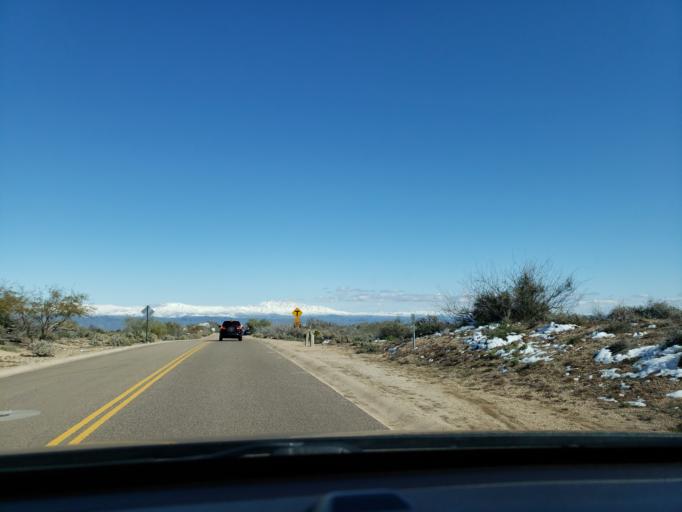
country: US
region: Arizona
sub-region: Maricopa County
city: Rio Verde
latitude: 33.7126
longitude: -111.8071
